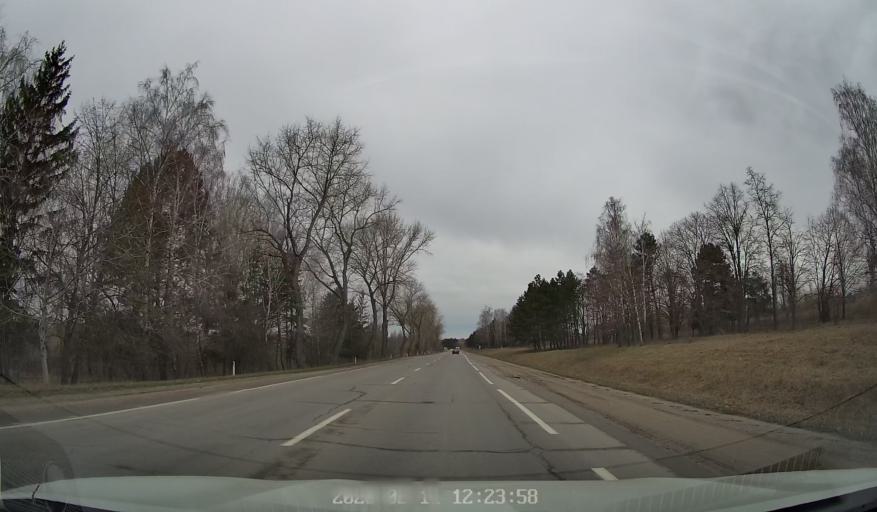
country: MD
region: Raionul Edinet
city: Edinet
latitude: 48.1427
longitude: 27.3523
